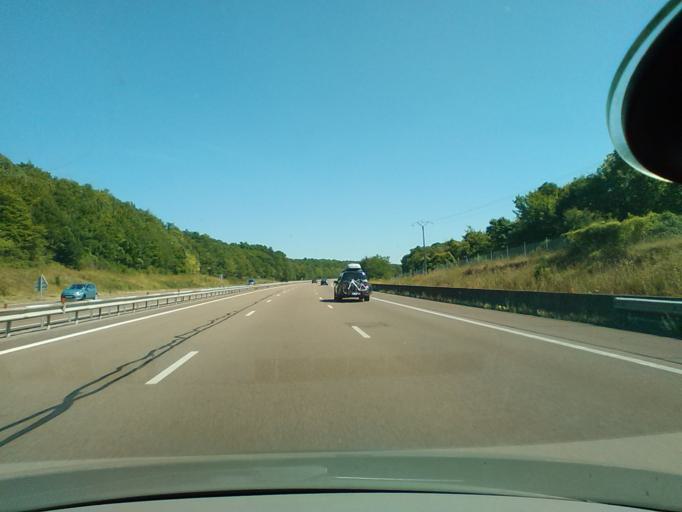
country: FR
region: Bourgogne
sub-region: Departement de l'Yonne
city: Aillant-sur-Tholon
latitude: 47.9253
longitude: 3.2768
